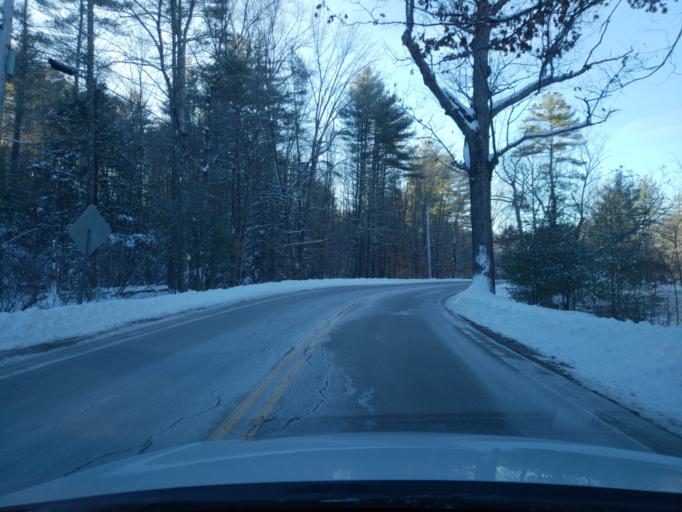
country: US
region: New Hampshire
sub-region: Hillsborough County
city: New Boston
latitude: 42.9952
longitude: -71.6697
